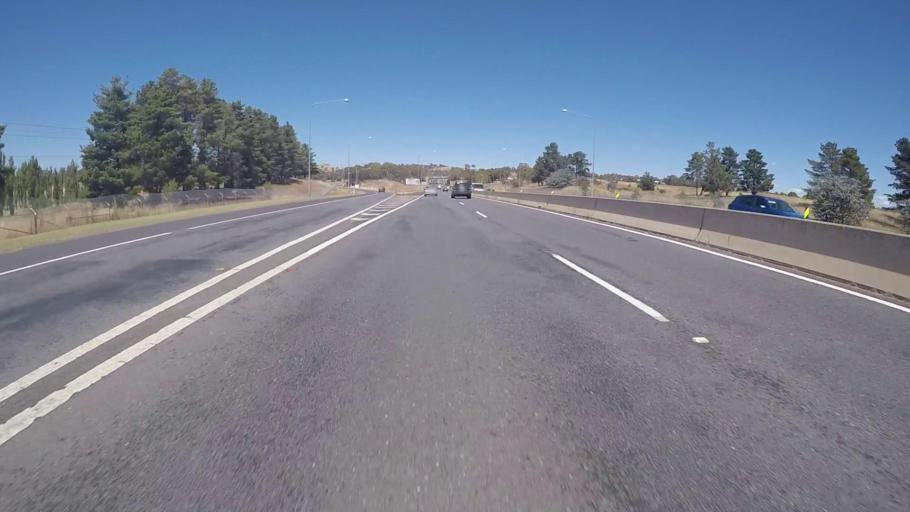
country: AU
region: Australian Capital Territory
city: Macquarie
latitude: -35.3157
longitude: 149.0629
